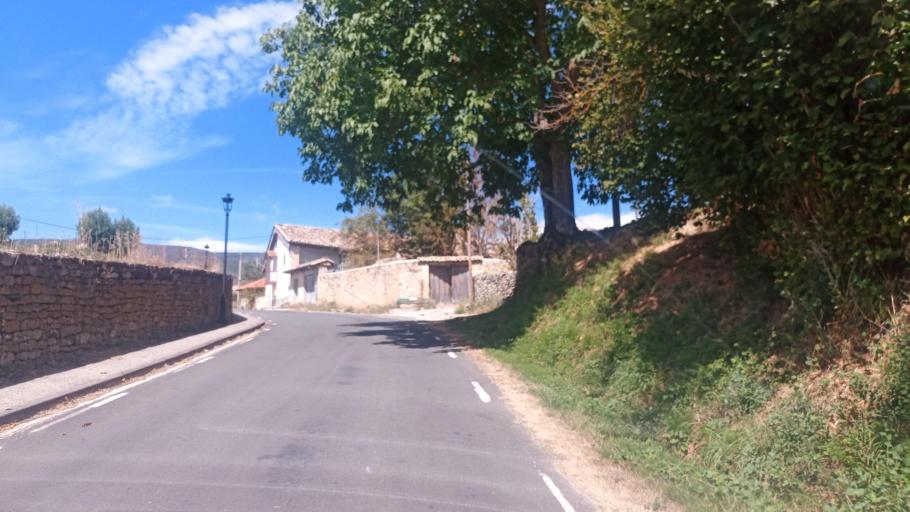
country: ES
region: Castille and Leon
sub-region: Provincia de Burgos
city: Espinosa de los Monteros
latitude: 43.0396
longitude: -3.6660
